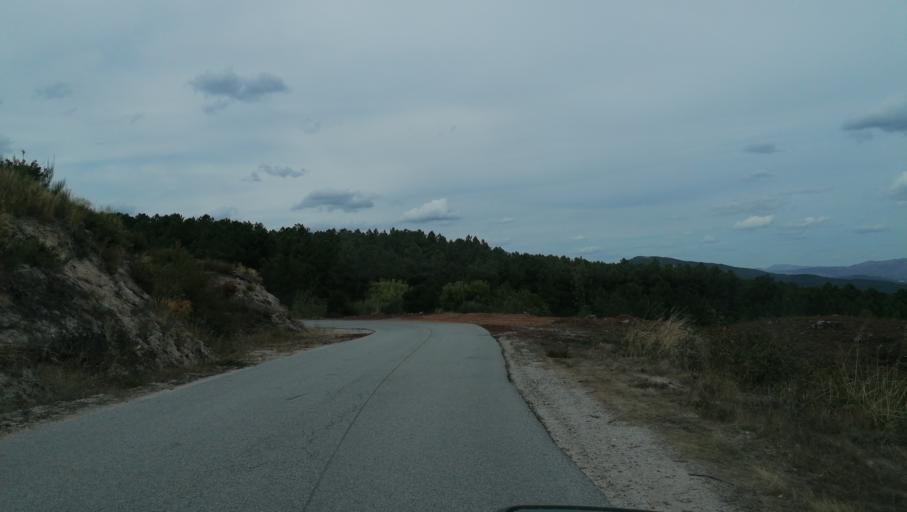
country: PT
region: Vila Real
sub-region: Vila Pouca de Aguiar
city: Vila Pouca de Aguiar
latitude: 41.5550
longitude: -7.6348
